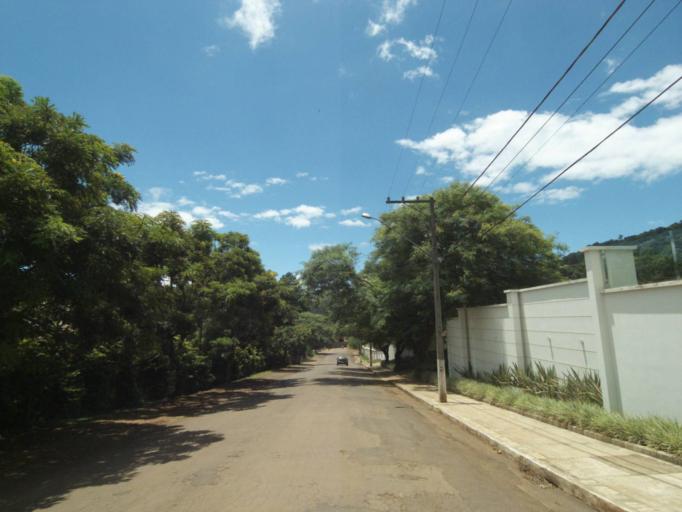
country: BR
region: Parana
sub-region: Uniao Da Vitoria
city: Uniao da Vitoria
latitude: -26.1622
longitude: -51.5531
